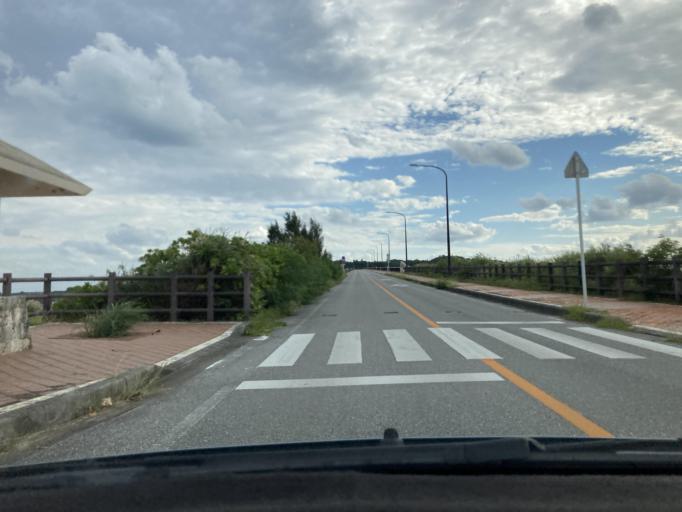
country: JP
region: Okinawa
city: Katsuren-haebaru
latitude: 26.3378
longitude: 127.9550
